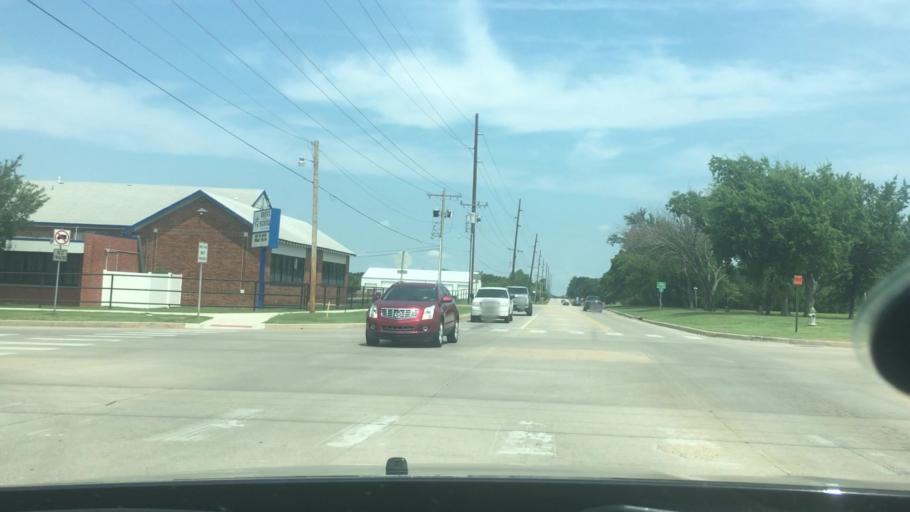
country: US
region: Oklahoma
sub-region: Pottawatomie County
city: Shawnee
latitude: 35.3615
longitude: -96.8943
